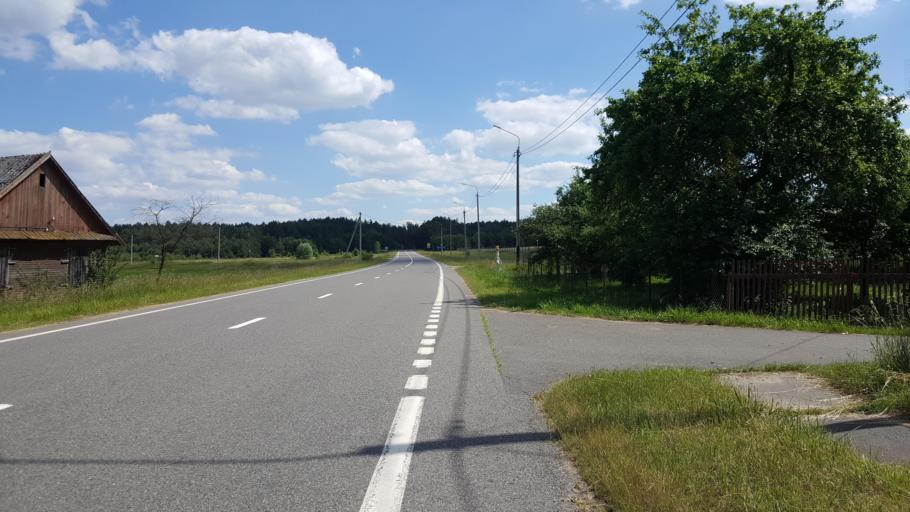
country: BY
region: Brest
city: Kamyanyuki
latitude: 52.5248
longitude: 23.6562
